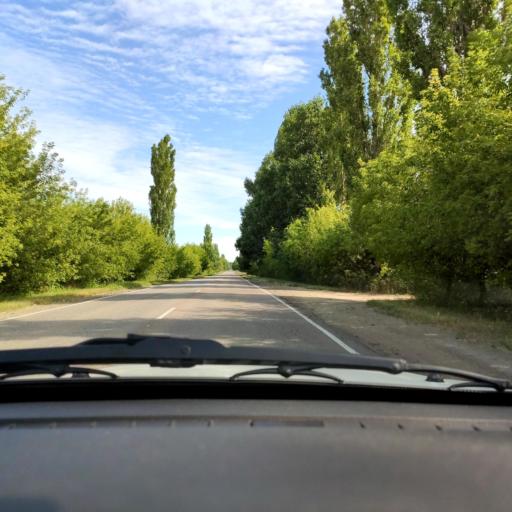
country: RU
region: Voronezj
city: Uglyanets
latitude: 51.8391
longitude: 39.6526
